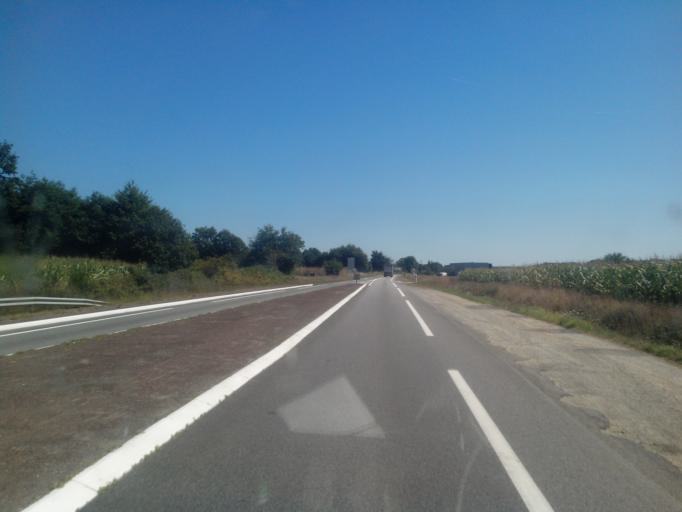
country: FR
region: Brittany
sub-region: Departement du Morbihan
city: Guegon
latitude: 47.9601
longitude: -2.5821
